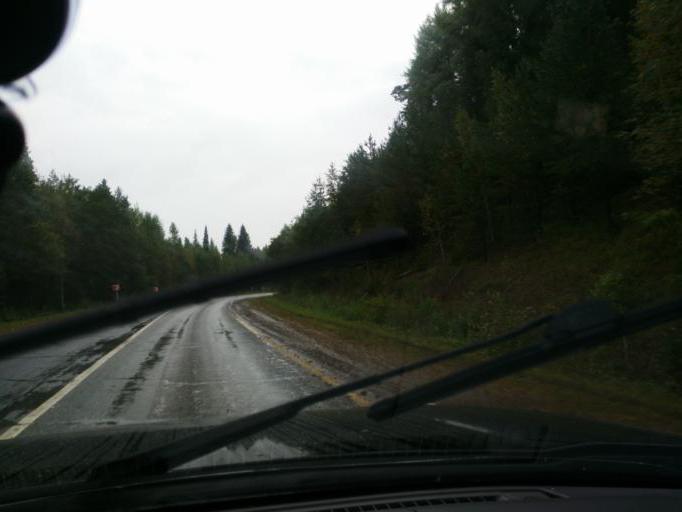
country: RU
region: Perm
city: Yugo-Kamskiy
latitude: 57.5261
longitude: 55.6840
